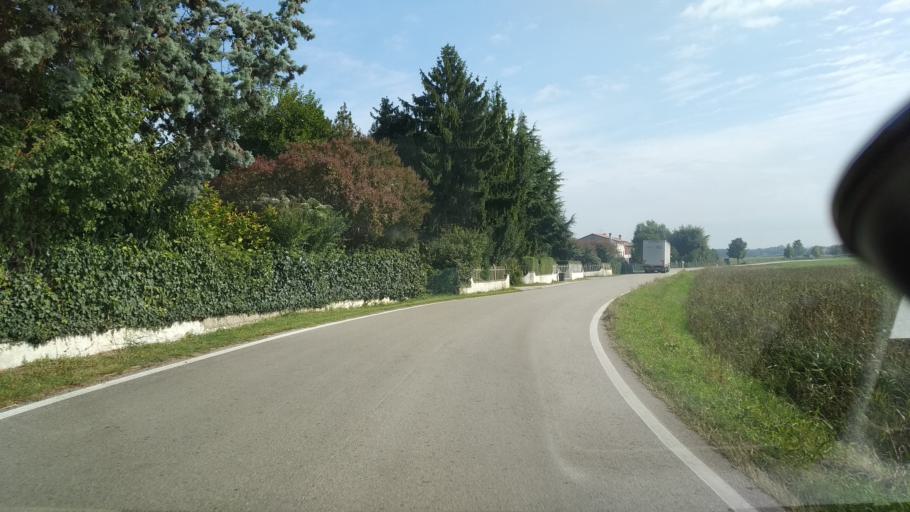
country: IT
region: Veneto
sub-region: Provincia di Vicenza
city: Mason Vicentino
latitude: 45.6975
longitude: 11.5886
